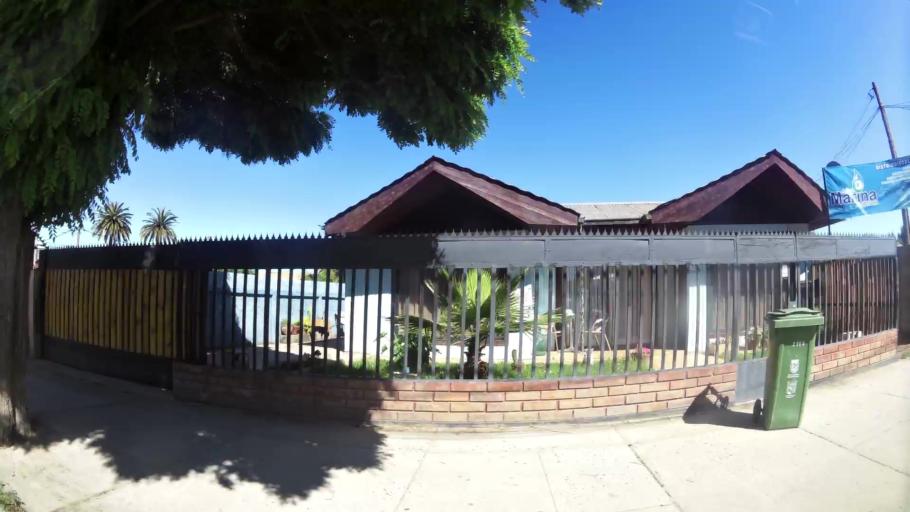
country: CL
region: Valparaiso
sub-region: Provincia de Marga Marga
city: Quilpue
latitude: -33.3188
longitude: -71.4074
